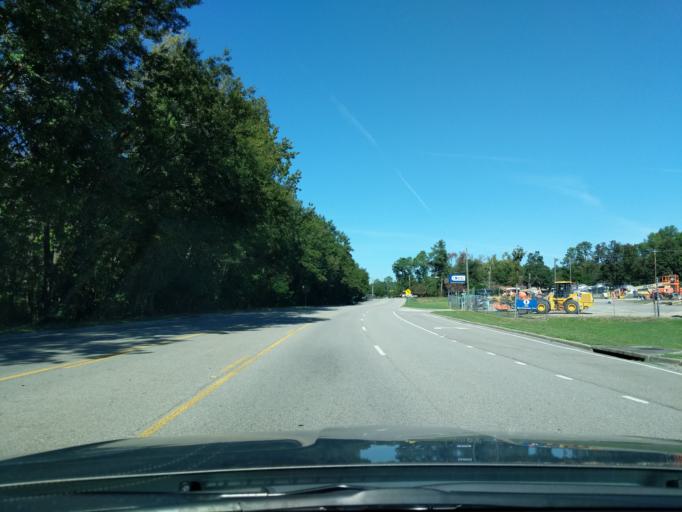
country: US
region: Georgia
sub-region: Richmond County
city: Augusta
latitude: 33.4319
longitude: -82.0080
